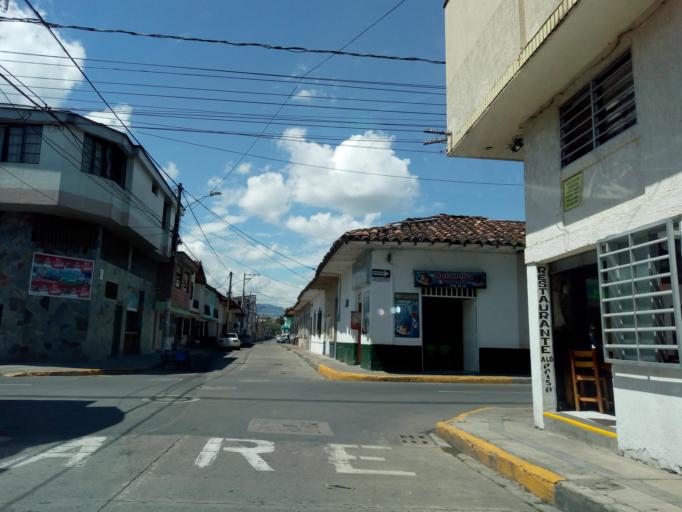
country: CO
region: Valle del Cauca
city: Cartago
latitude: 4.7505
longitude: -75.9074
